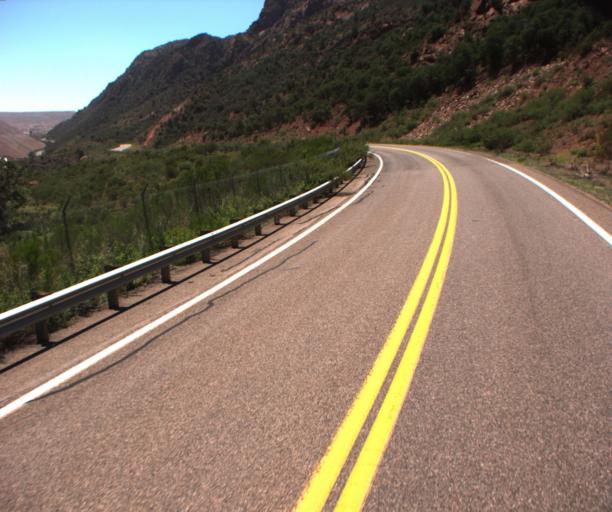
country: US
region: Arizona
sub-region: Greenlee County
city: Morenci
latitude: 33.1542
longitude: -109.3742
